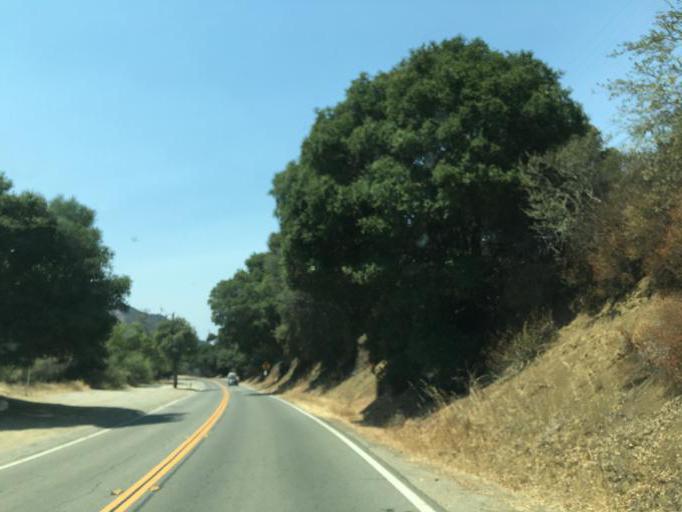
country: US
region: California
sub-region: Los Angeles County
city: Malibu Beach
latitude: 34.0813
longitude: -118.7021
